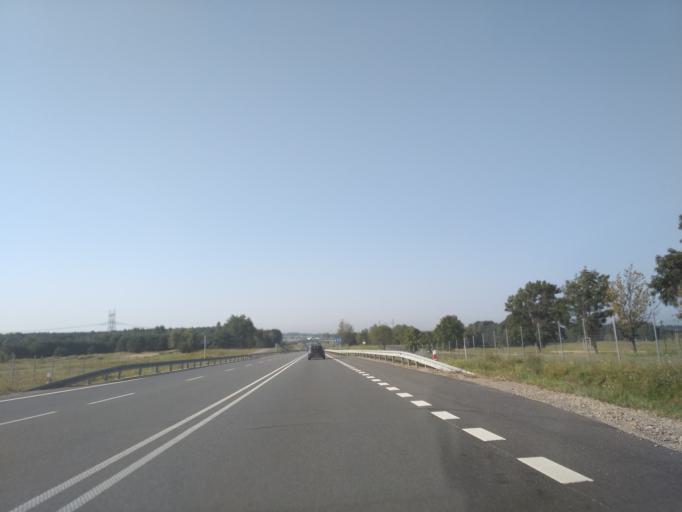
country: PL
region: Subcarpathian Voivodeship
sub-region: Powiat rzeszowski
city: Sokolow Malopolski
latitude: 50.1814
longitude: 22.0943
